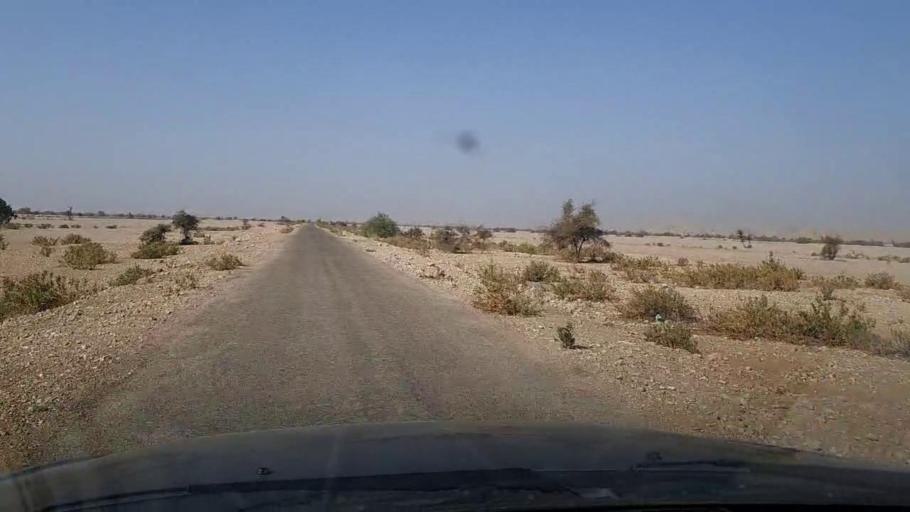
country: PK
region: Sindh
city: Sann
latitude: 25.8968
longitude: 67.9953
